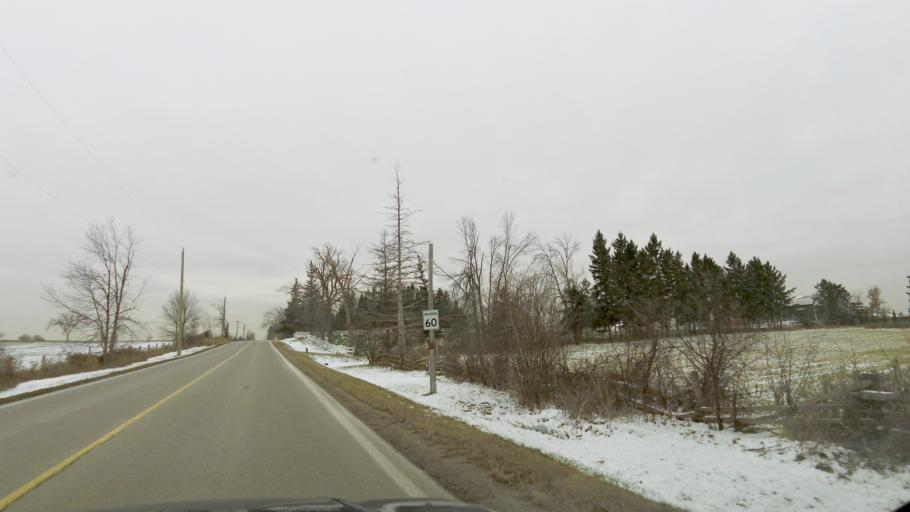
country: CA
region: Ontario
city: Vaughan
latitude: 43.8642
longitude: -79.5920
